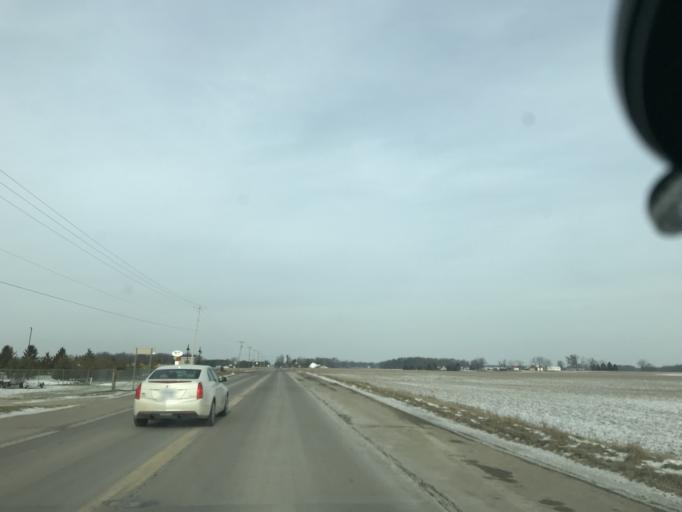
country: US
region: Michigan
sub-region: Ionia County
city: Lake Odessa
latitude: 42.7646
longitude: -85.0743
